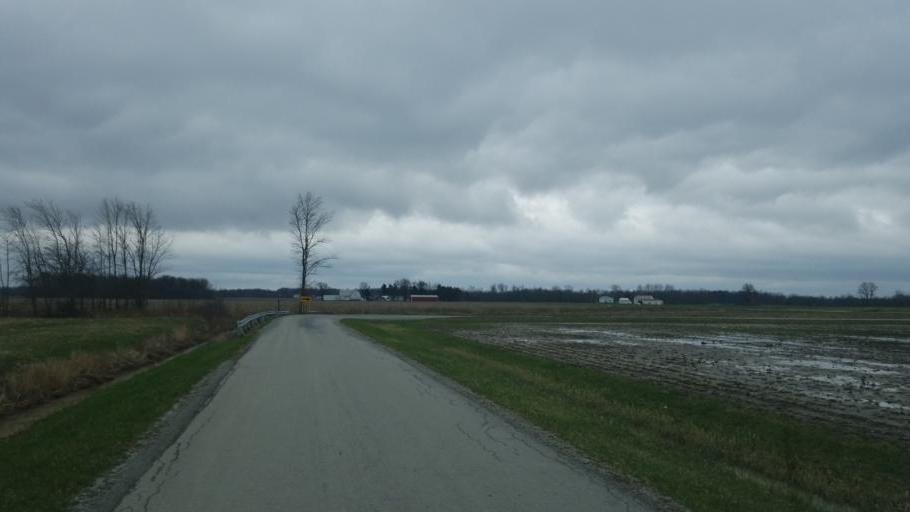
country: US
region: Ohio
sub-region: Hardin County
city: Forest
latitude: 40.7312
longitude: -83.4583
